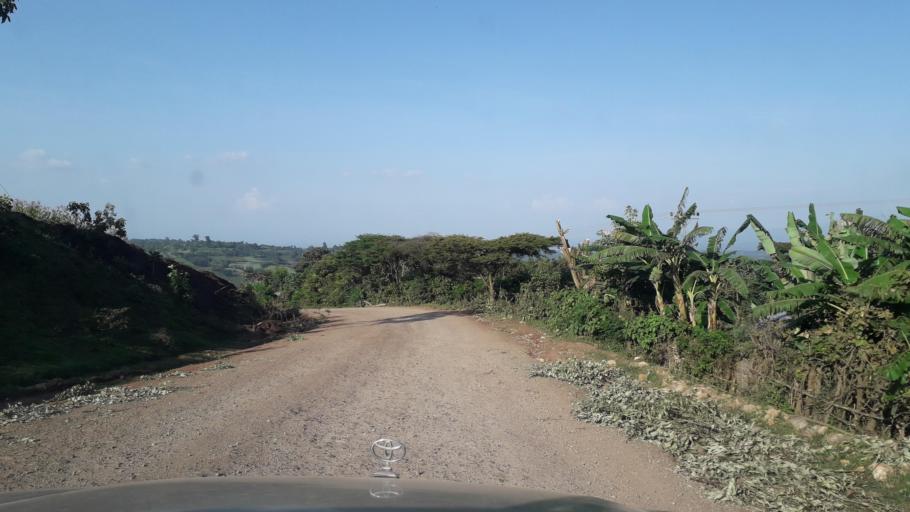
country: ET
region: Oromiya
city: Jima
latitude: 7.4693
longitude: 36.8757
